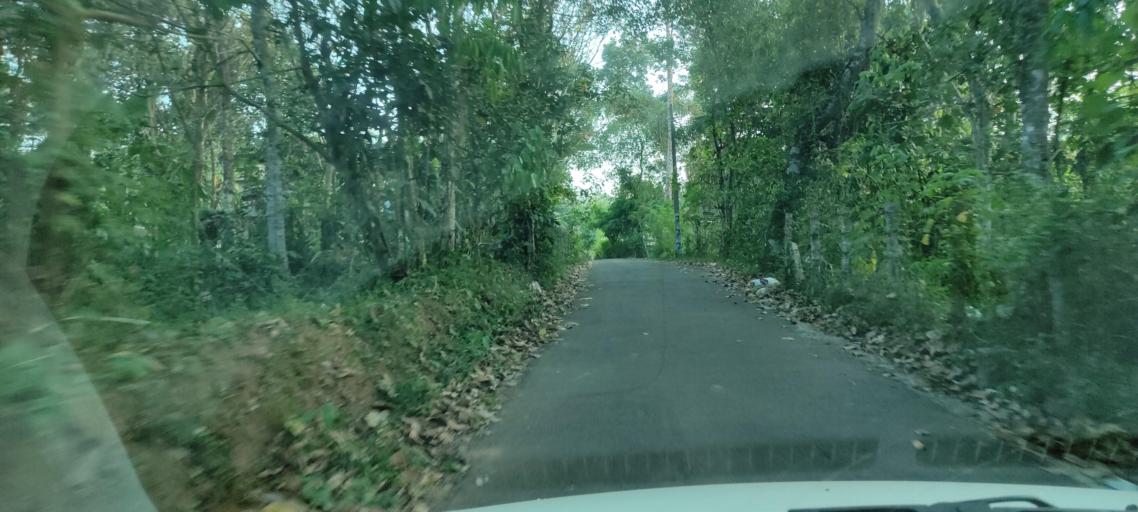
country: IN
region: Kerala
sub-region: Alappuzha
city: Kattanam
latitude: 9.1634
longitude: 76.5908
